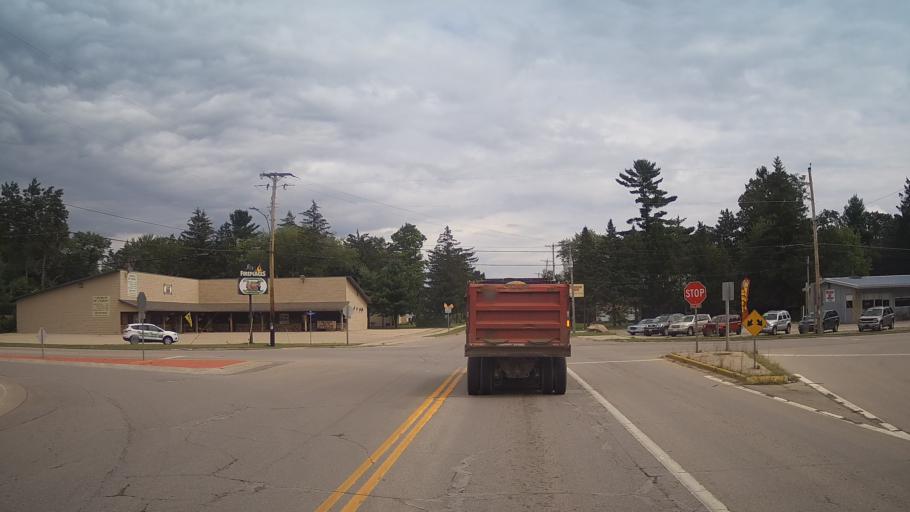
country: US
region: Wisconsin
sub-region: Waushara County
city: Wautoma
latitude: 44.0680
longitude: -89.2979
